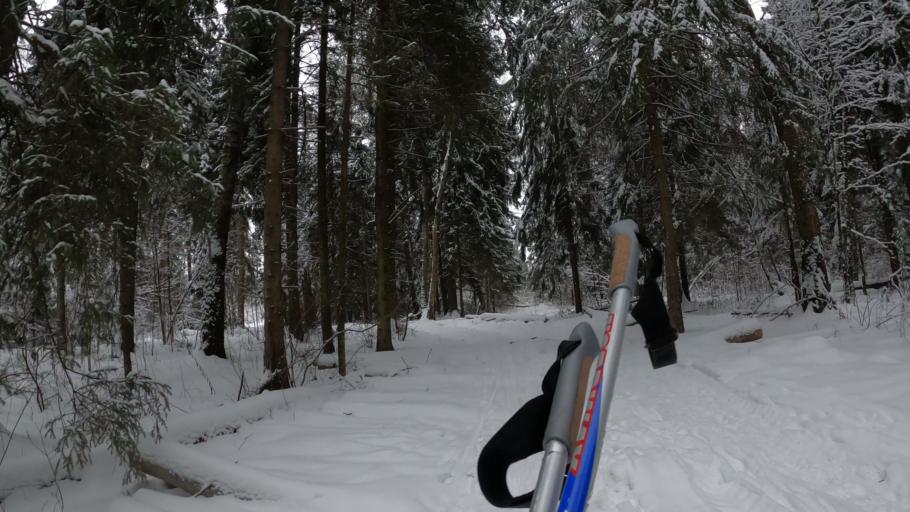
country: RU
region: Moskovskaya
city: Firsanovka
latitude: 55.9550
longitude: 37.2213
